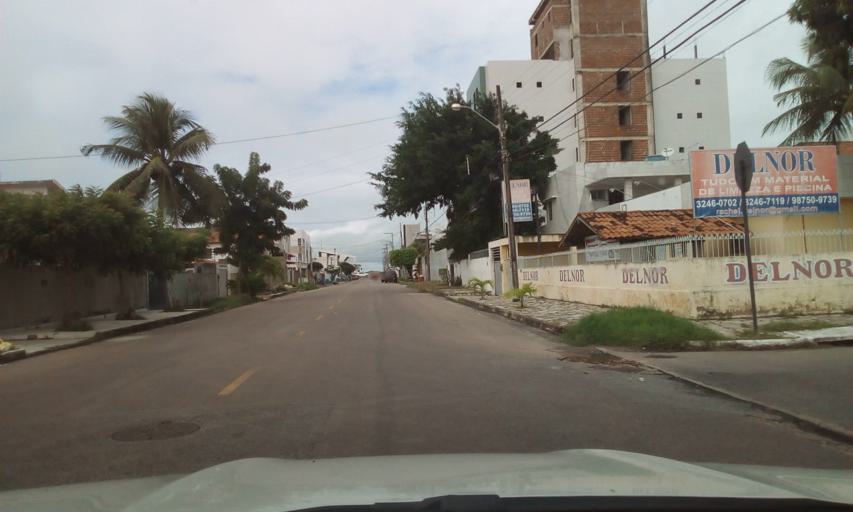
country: BR
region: Paraiba
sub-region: Joao Pessoa
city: Joao Pessoa
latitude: -7.0593
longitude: -34.8457
